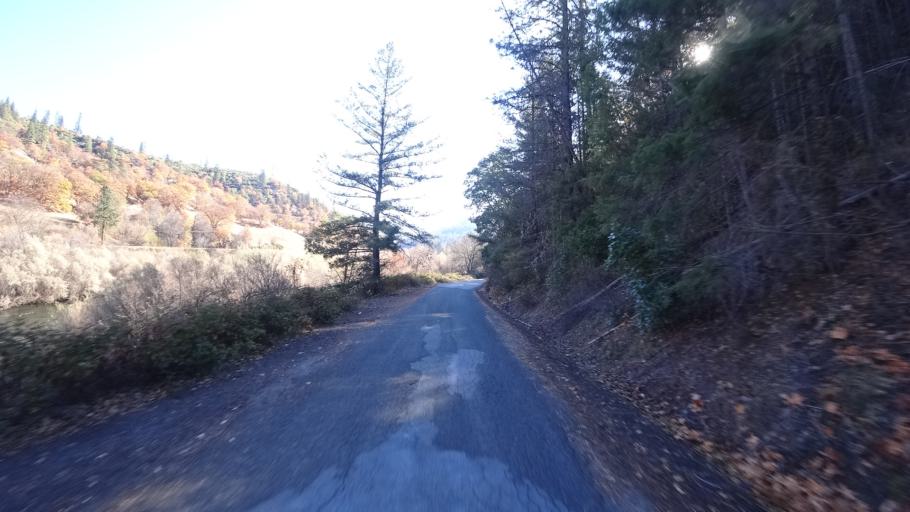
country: US
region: California
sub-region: Siskiyou County
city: Yreka
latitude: 41.8458
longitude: -122.9029
